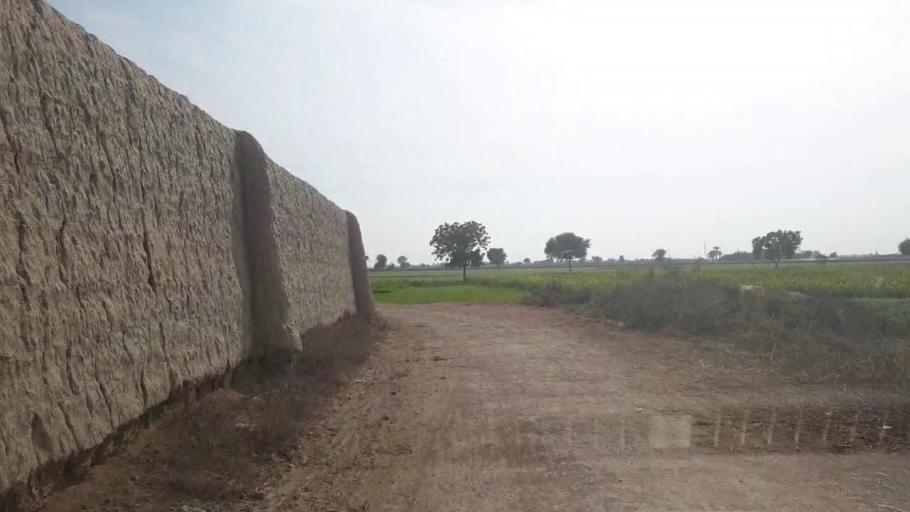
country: PK
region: Sindh
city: Nawabshah
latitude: 26.0922
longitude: 68.4862
